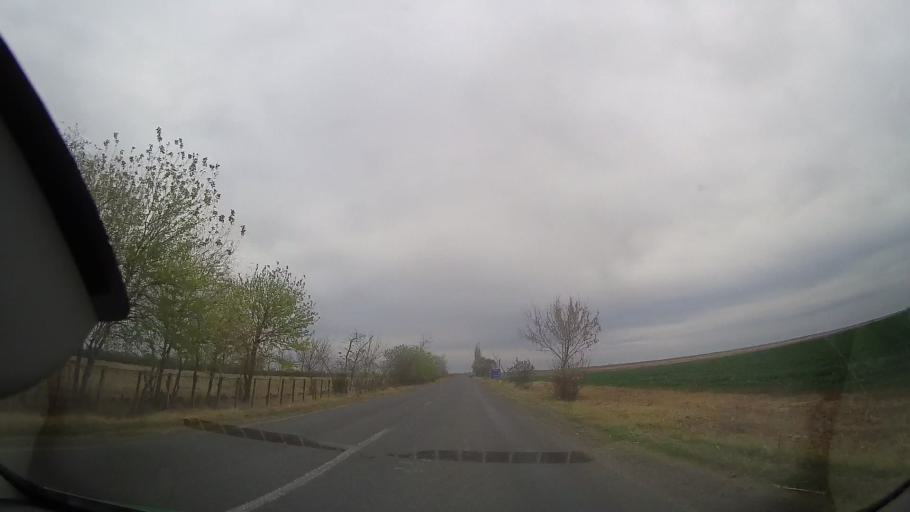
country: RO
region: Buzau
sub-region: Comuna Padina
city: Padina
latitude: 44.8193
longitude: 27.1197
